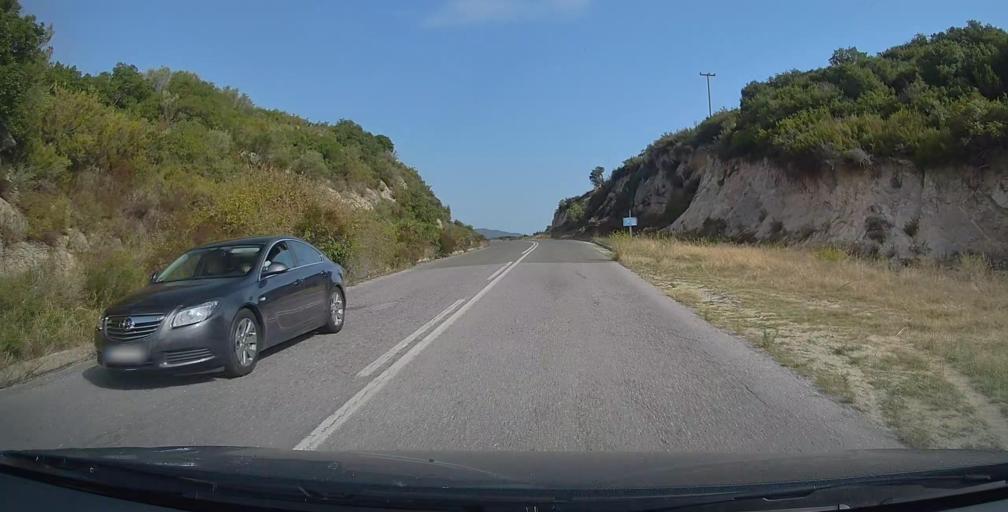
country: GR
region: Central Macedonia
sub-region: Nomos Chalkidikis
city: Sykia
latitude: 40.0044
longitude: 23.9831
